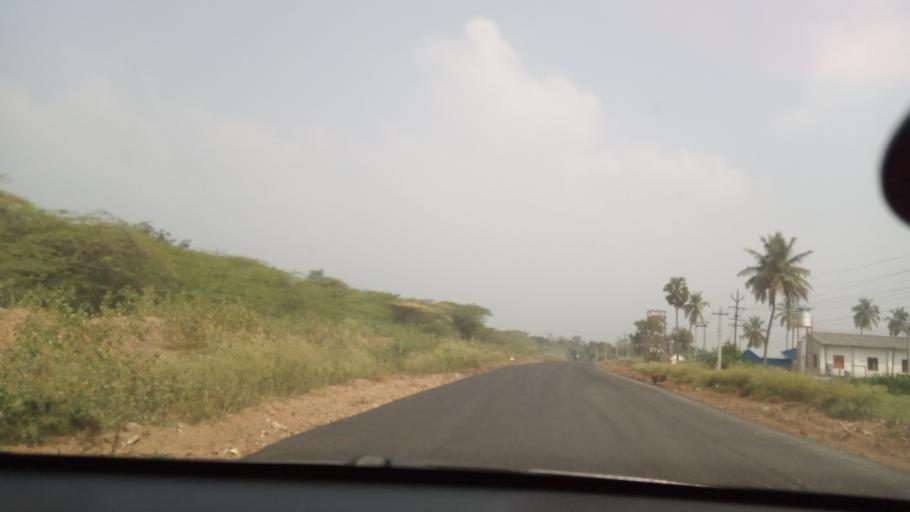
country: IN
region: Tamil Nadu
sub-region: Erode
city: Sathyamangalam
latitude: 11.5416
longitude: 77.1387
